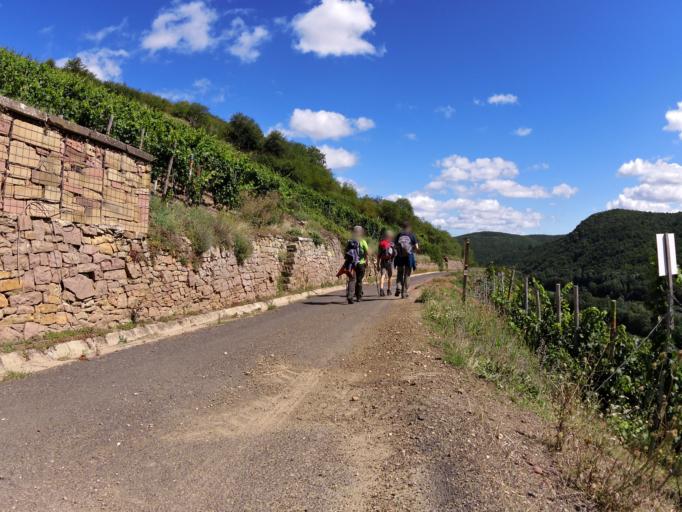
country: DE
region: Rheinland-Pfalz
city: Niederhausen
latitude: 49.7926
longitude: 7.7680
